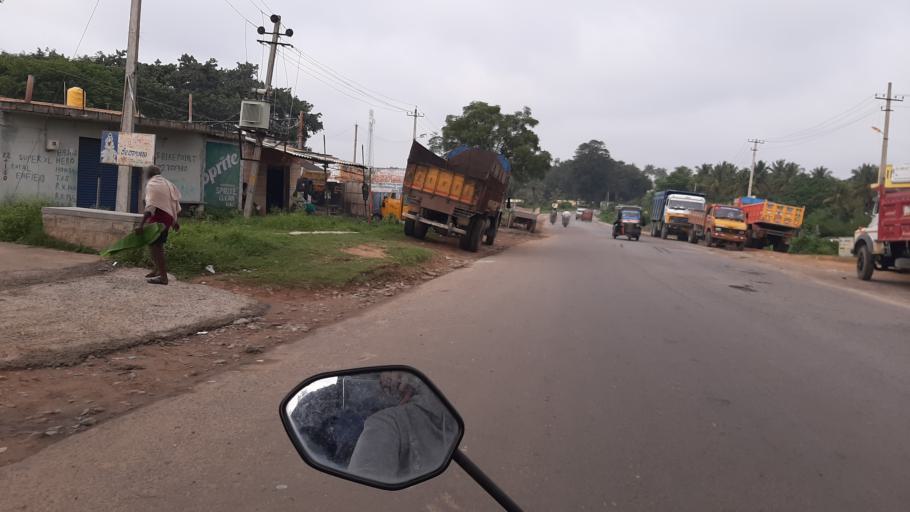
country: IN
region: Karnataka
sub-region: Bangalore Rural
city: Nelamangala
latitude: 12.9708
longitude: 77.4148
